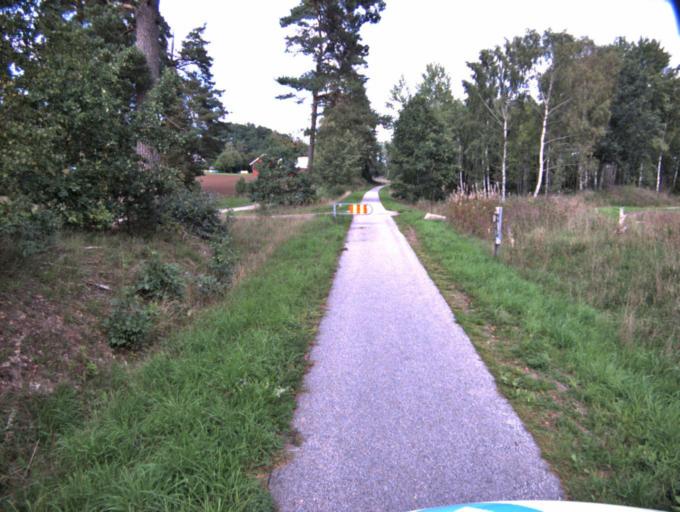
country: SE
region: Vaestra Goetaland
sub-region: Ulricehamns Kommun
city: Ulricehamn
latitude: 57.8434
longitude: 13.4218
